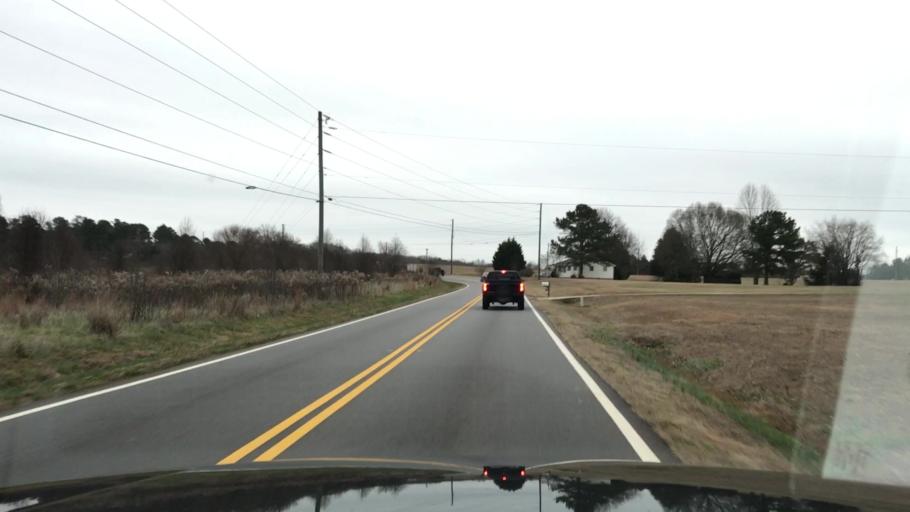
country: US
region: Georgia
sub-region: Walton County
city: Monroe
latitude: 33.8760
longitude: -83.7679
